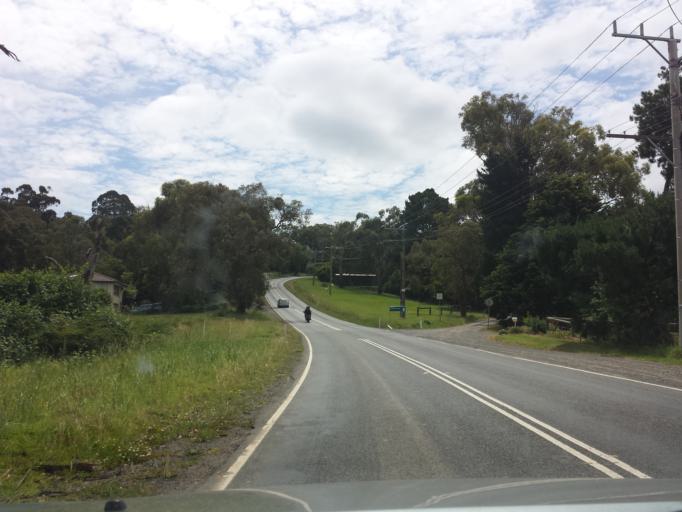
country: AU
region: Victoria
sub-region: Yarra Ranges
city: Belgrave Heights
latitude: -37.9378
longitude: 145.3572
